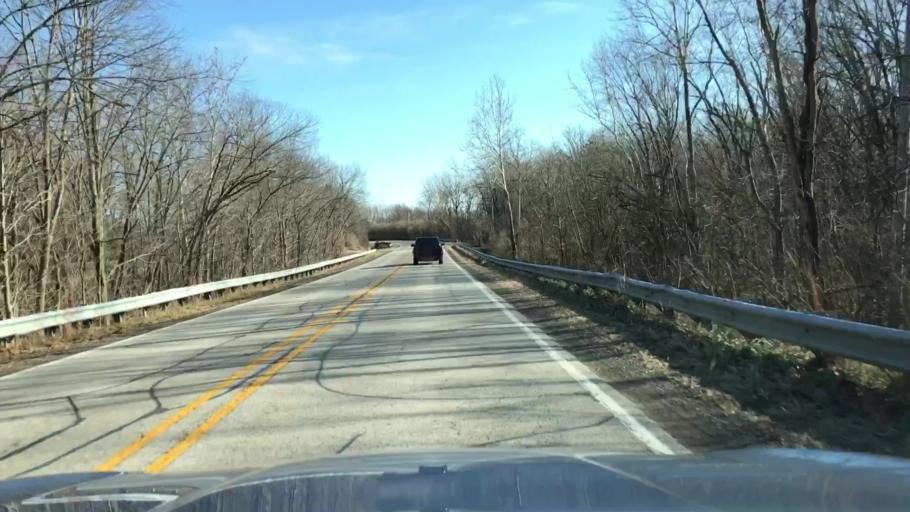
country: US
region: Illinois
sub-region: McLean County
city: Lexington
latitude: 40.6467
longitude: -88.8387
